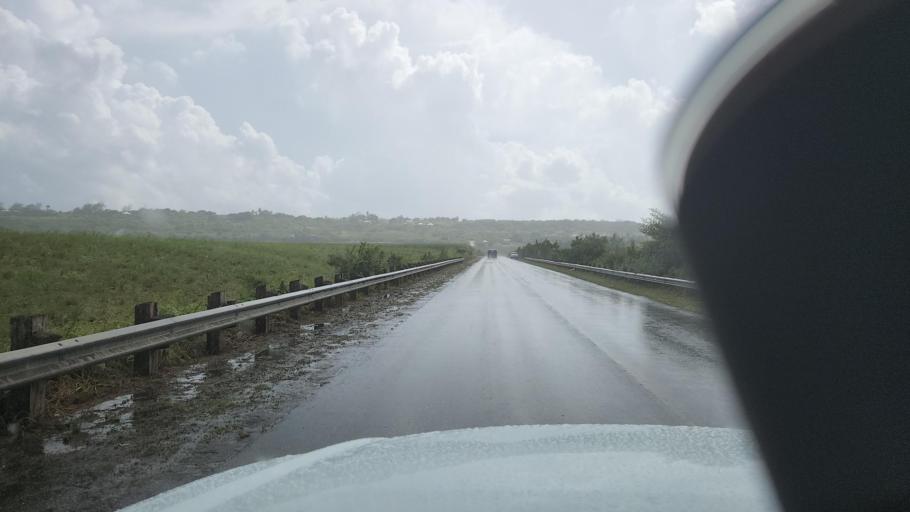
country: BB
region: Saint Michael
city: Bridgetown
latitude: 13.1190
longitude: -59.5628
